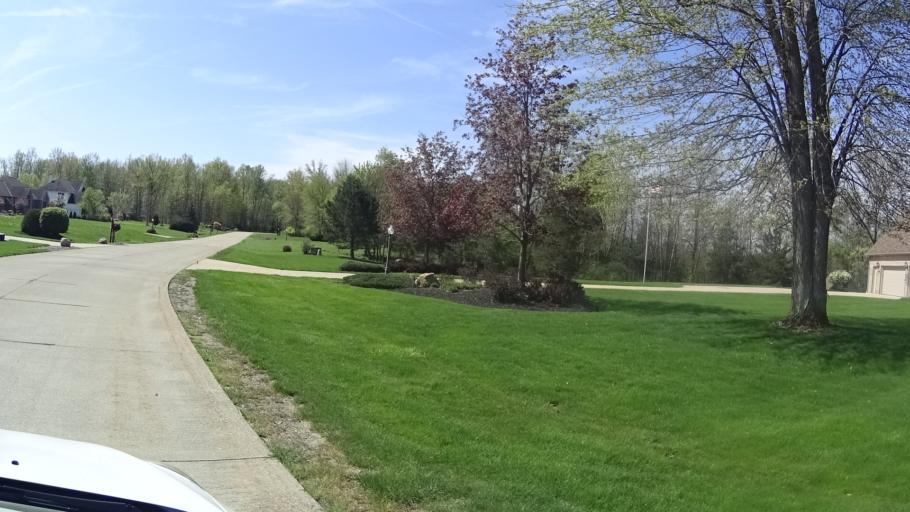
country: US
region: Ohio
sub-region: Lorain County
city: Lagrange
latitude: 41.2975
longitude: -82.1268
